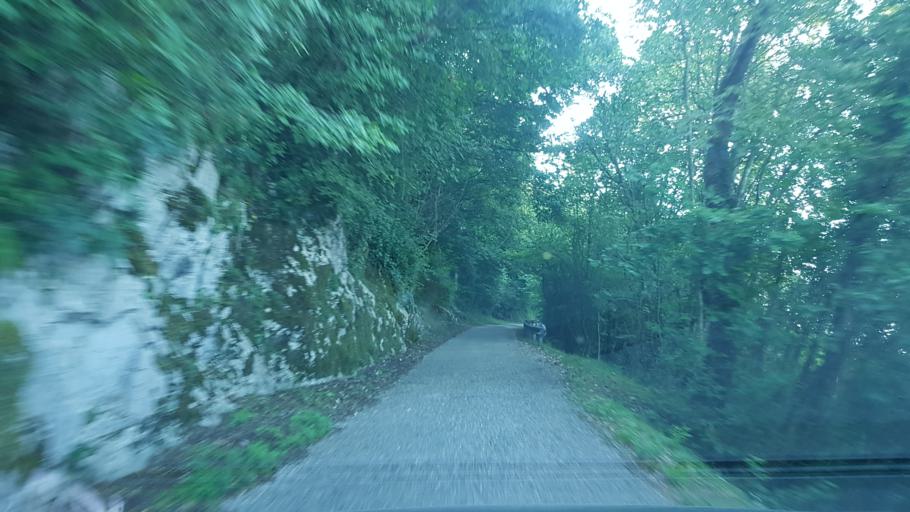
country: IT
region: Friuli Venezia Giulia
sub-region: Provincia di Udine
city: Nimis
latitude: 46.2340
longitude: 13.2497
